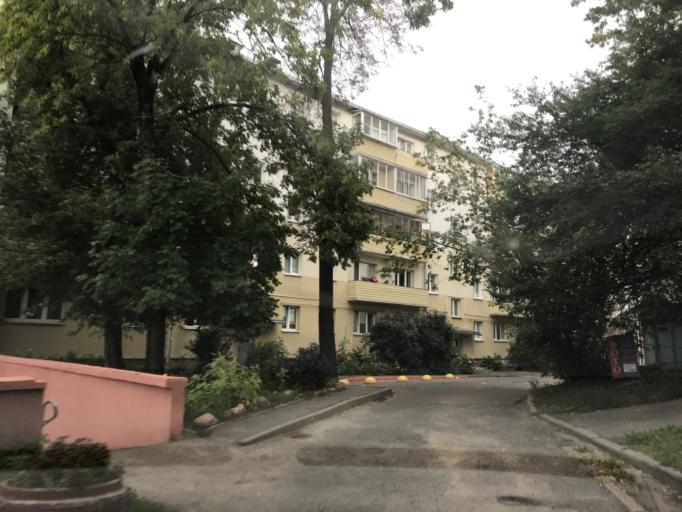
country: BY
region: Minsk
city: Minsk
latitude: 53.9127
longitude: 27.5917
